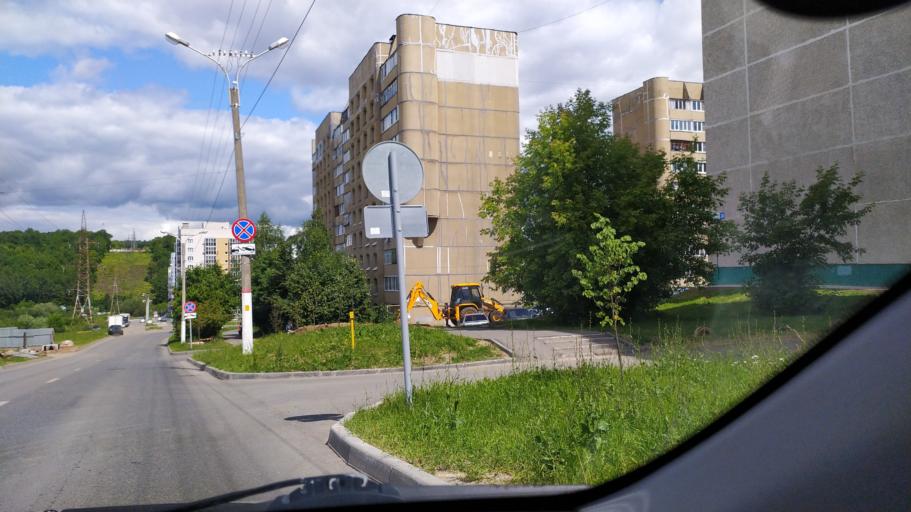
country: RU
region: Chuvashia
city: Novyye Lapsary
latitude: 56.1201
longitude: 47.1748
